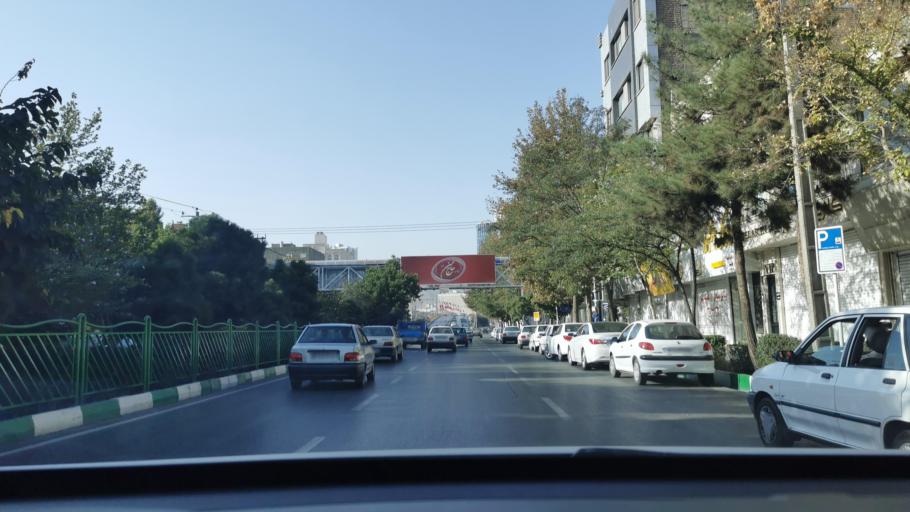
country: IR
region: Razavi Khorasan
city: Mashhad
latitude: 36.3309
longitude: 59.5031
